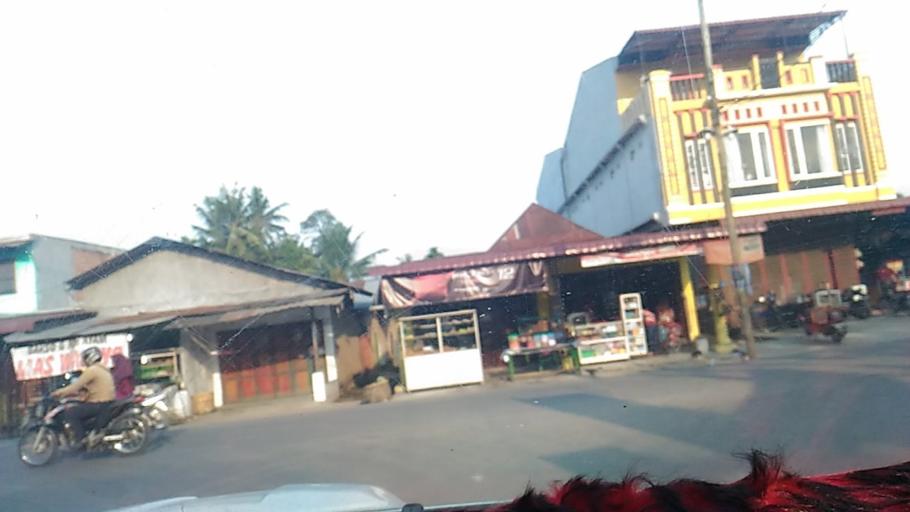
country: ID
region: North Sumatra
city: Labuhan Deli
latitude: 3.7065
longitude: 98.6003
